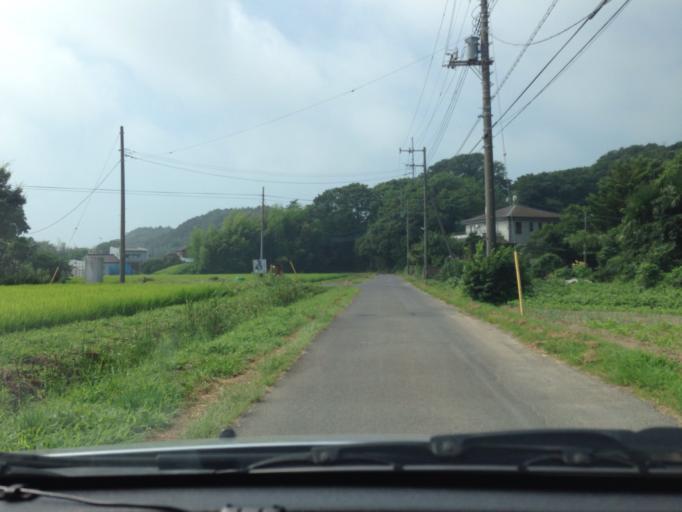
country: JP
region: Ibaraki
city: Inashiki
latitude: 36.0129
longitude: 140.3622
